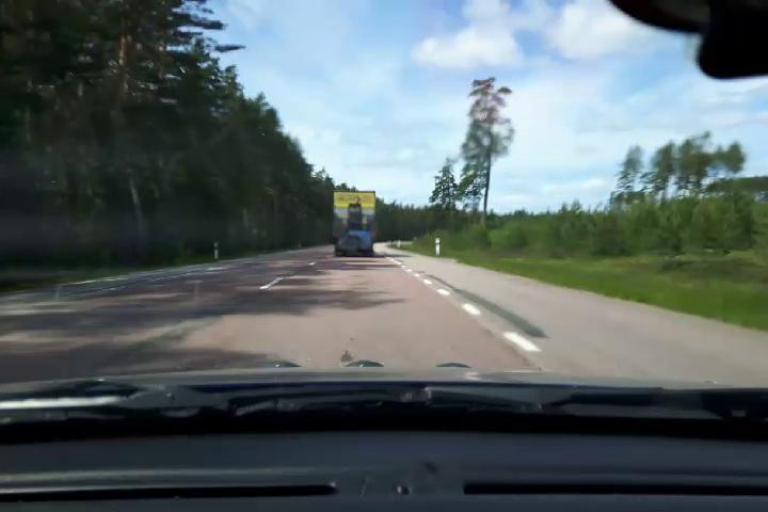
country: SE
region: Uppsala
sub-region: Osthammars Kommun
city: Bjorklinge
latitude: 60.1187
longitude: 17.5143
